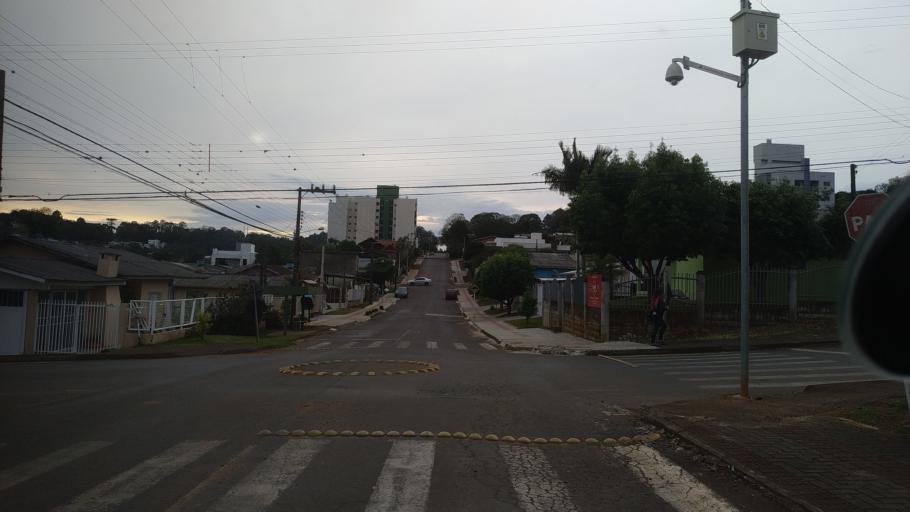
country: BR
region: Santa Catarina
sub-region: Chapeco
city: Chapeco
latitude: -27.1180
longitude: -52.6003
